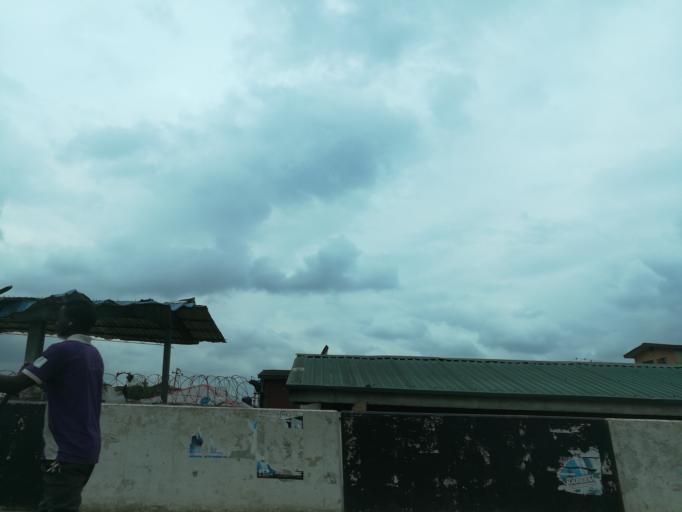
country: NG
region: Lagos
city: Ojota
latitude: 6.6156
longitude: 3.3972
